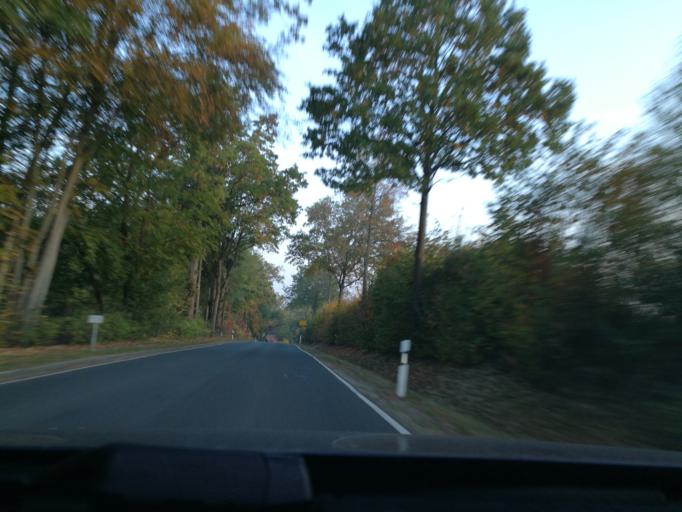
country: DE
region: Bavaria
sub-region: Regierungsbezirk Mittelfranken
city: Obermichelbach
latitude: 49.5540
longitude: 10.9149
